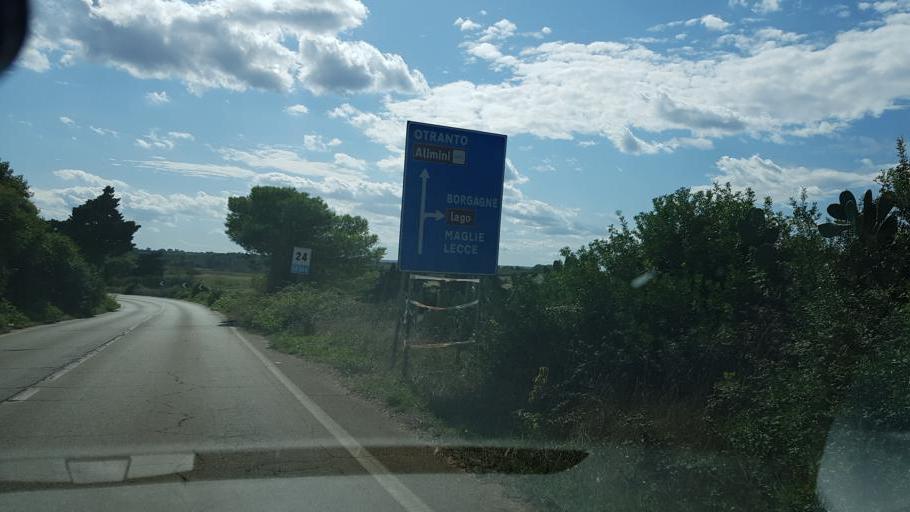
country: IT
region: Apulia
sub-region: Provincia di Lecce
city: Borgagne
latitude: 40.2254
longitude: 18.4414
